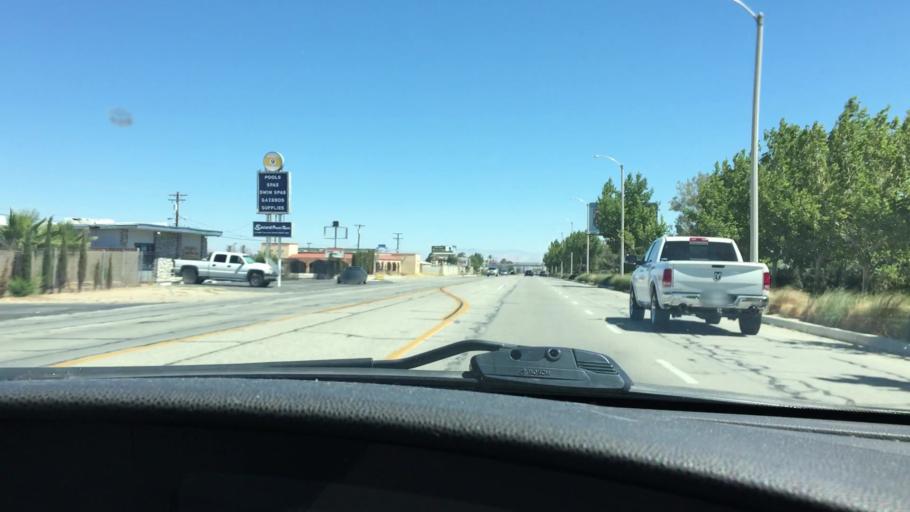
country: US
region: California
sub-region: Los Angeles County
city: Lancaster
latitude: 34.6524
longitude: -118.1293
